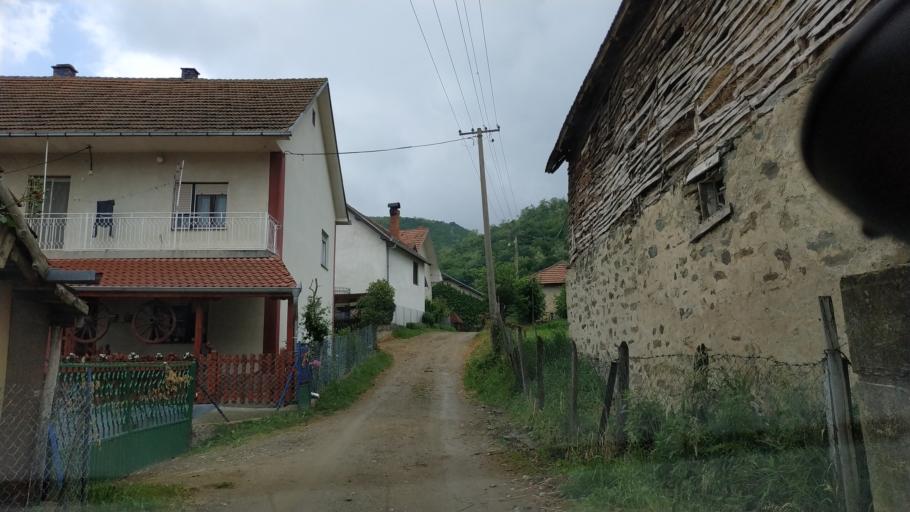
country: RS
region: Central Serbia
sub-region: Toplicki Okrug
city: Prokuplje
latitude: 43.4023
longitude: 21.5481
